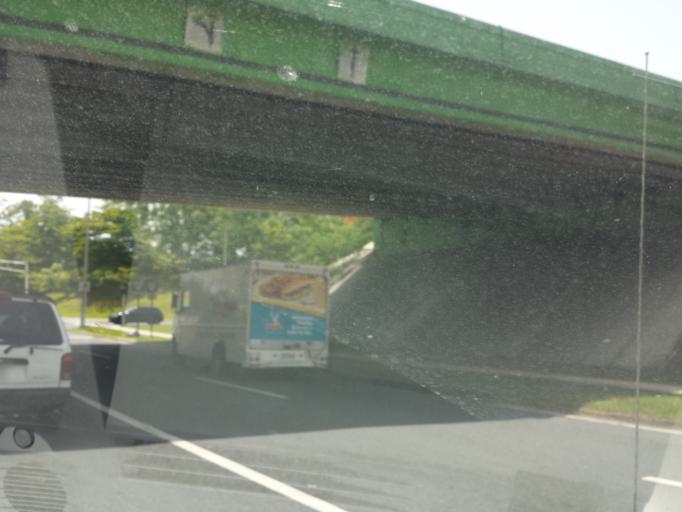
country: PR
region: Guaynabo
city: Guaynabo
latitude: 18.3943
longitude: -66.1029
